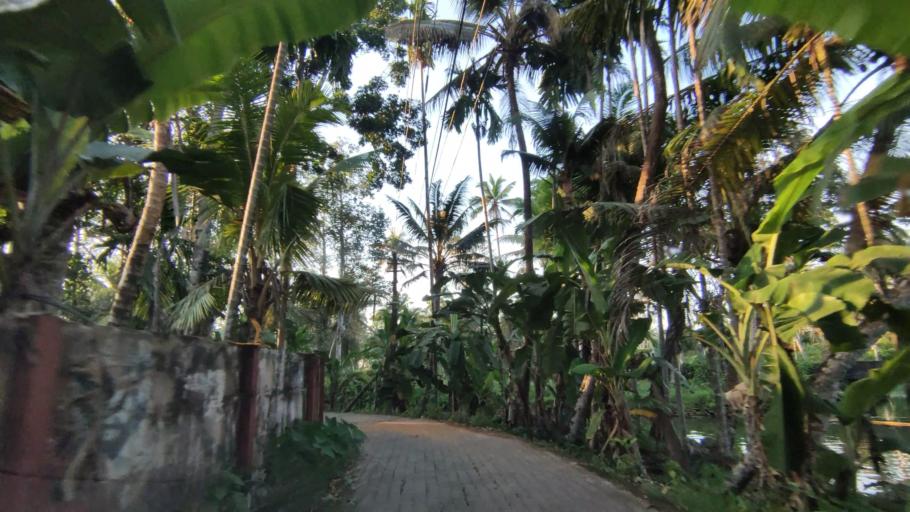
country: IN
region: Kerala
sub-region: Kottayam
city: Kottayam
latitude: 9.6307
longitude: 76.4850
